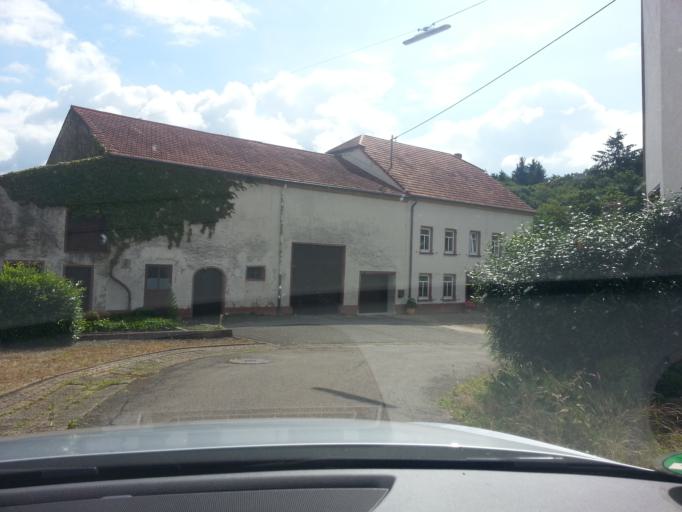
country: DE
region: Rheinland-Pfalz
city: Kirf
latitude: 49.5133
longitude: 6.4839
